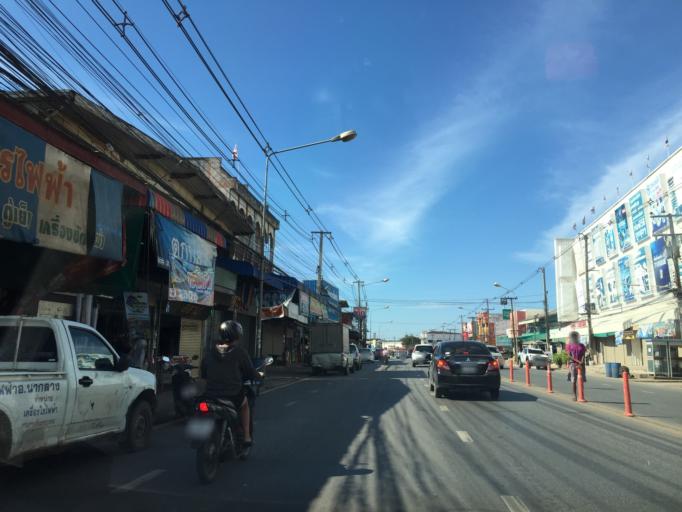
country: TH
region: Changwat Nong Bua Lamphu
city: Na Klang
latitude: 17.3010
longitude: 102.2053
